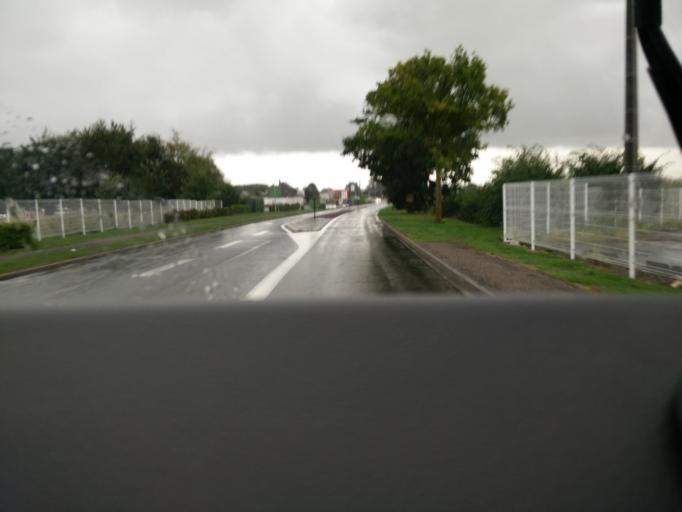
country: FR
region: Nord-Pas-de-Calais
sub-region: Departement du Pas-de-Calais
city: Savy-Berlette
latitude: 50.3548
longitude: 2.4846
